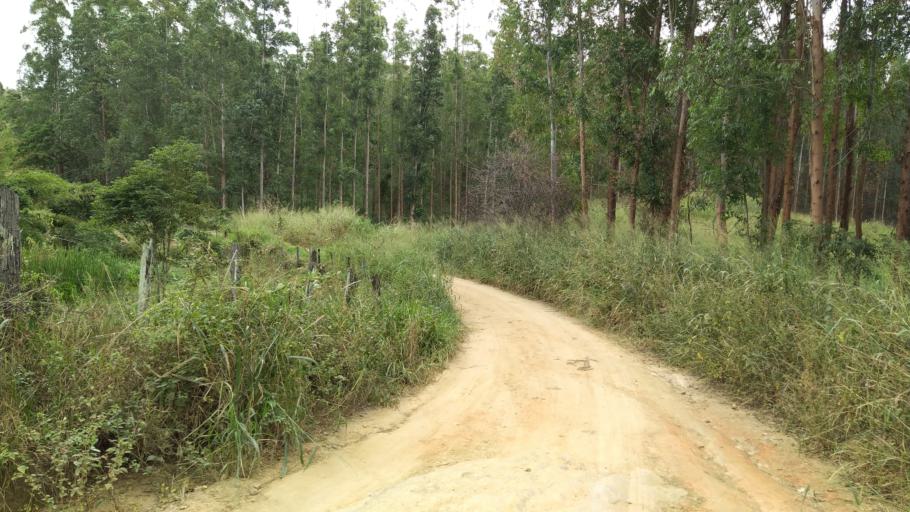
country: BR
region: Minas Gerais
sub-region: Almenara
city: Almenara
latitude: -16.6300
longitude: -40.4561
